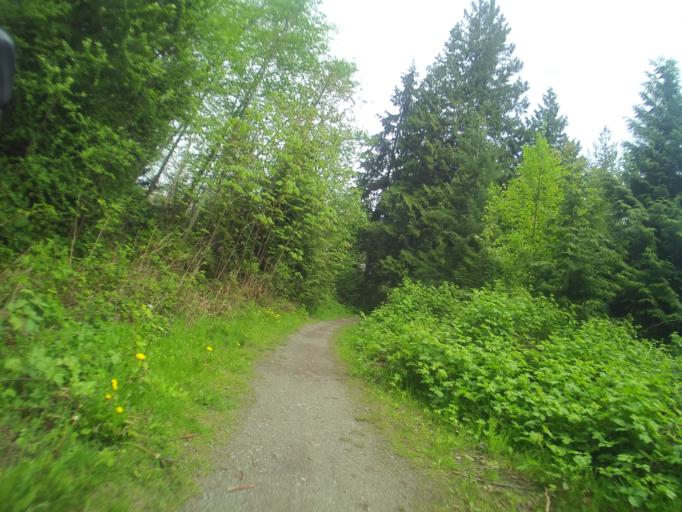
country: CA
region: British Columbia
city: West End
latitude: 49.2496
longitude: -123.2303
